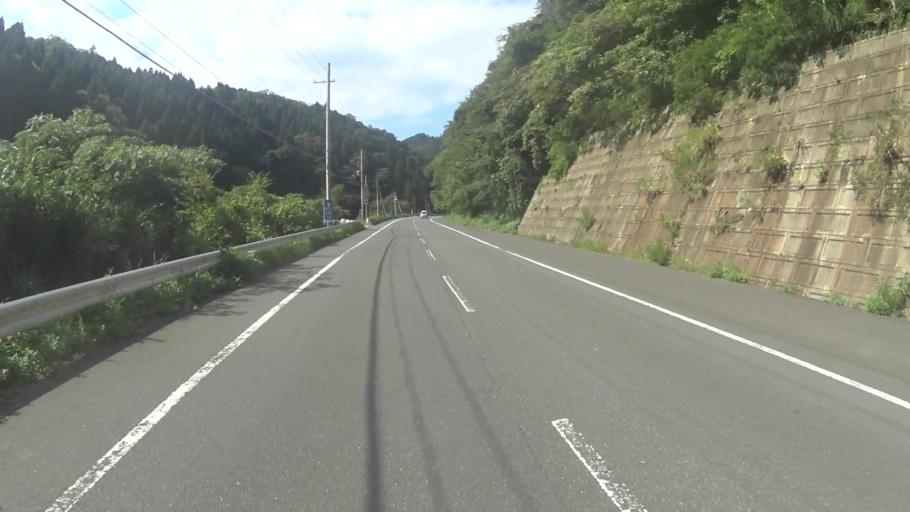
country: JP
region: Kyoto
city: Miyazu
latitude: 35.7334
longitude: 135.2572
